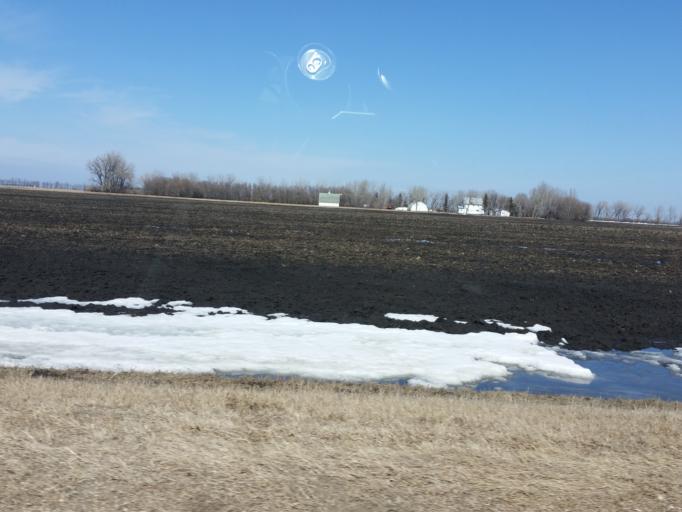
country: US
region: North Dakota
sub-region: Walsh County
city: Grafton
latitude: 48.4265
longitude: -97.2536
